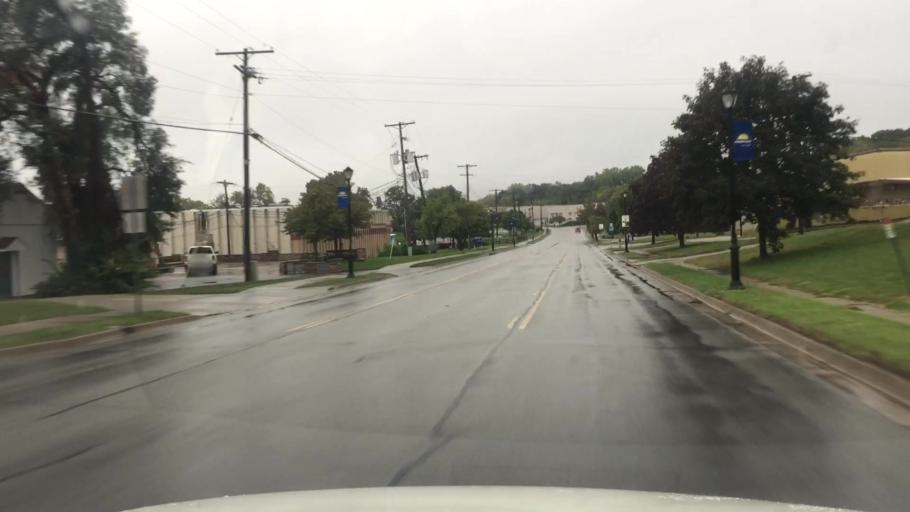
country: US
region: Kansas
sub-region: Johnson County
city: Merriam
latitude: 39.0366
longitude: -94.6886
